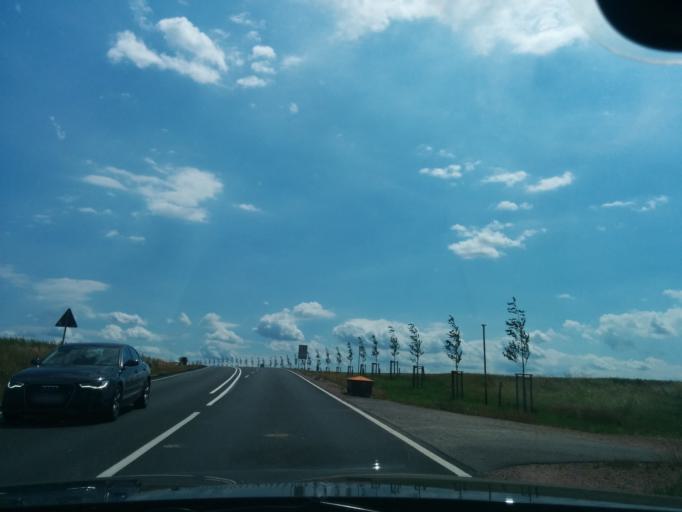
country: DE
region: Saxony
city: Hainichen
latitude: 51.0235
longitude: 13.1168
